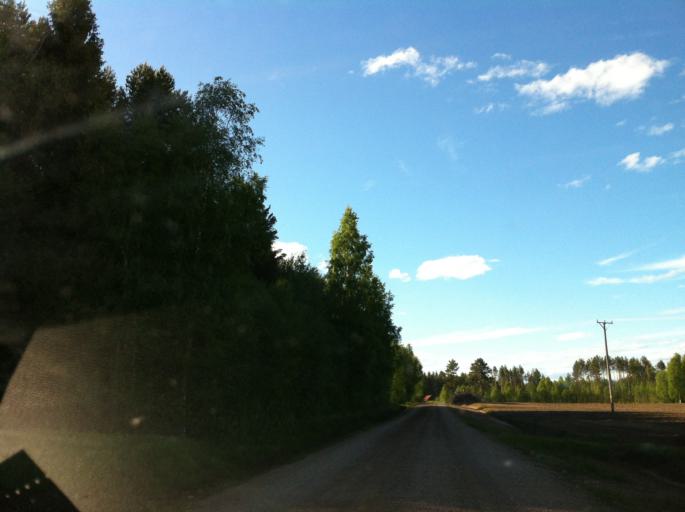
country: SE
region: Dalarna
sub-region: Leksand Municipality
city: Siljansnas
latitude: 60.7746
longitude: 14.8372
